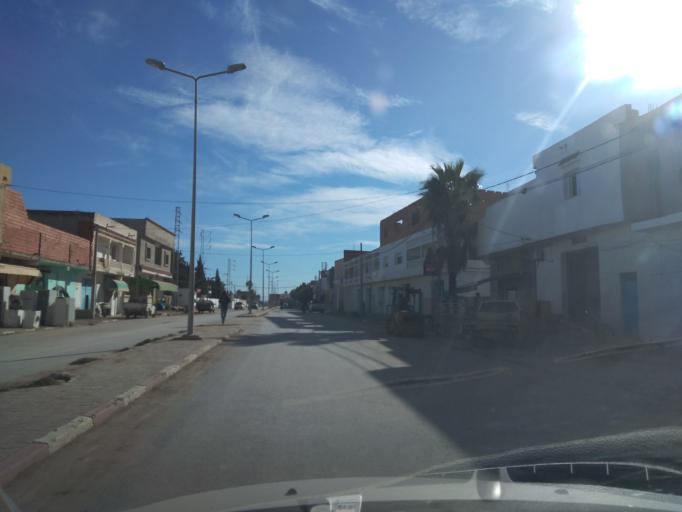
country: TN
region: Ariana
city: Qal'at al Andalus
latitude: 37.0587
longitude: 10.1197
